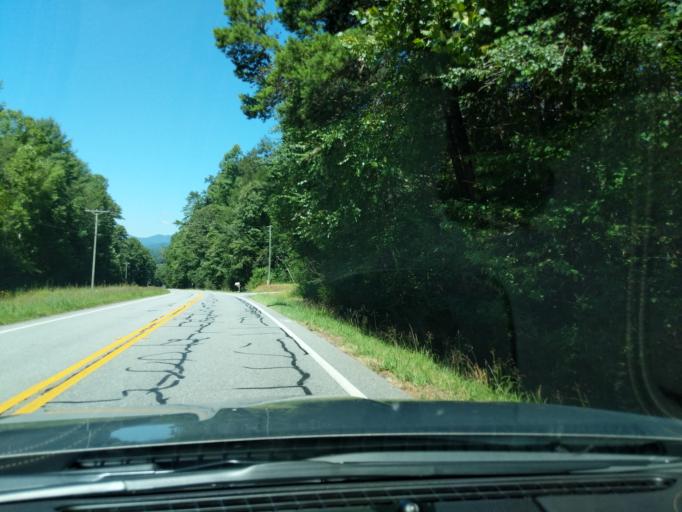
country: US
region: Georgia
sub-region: White County
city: Cleveland
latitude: 34.6763
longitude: -83.6594
